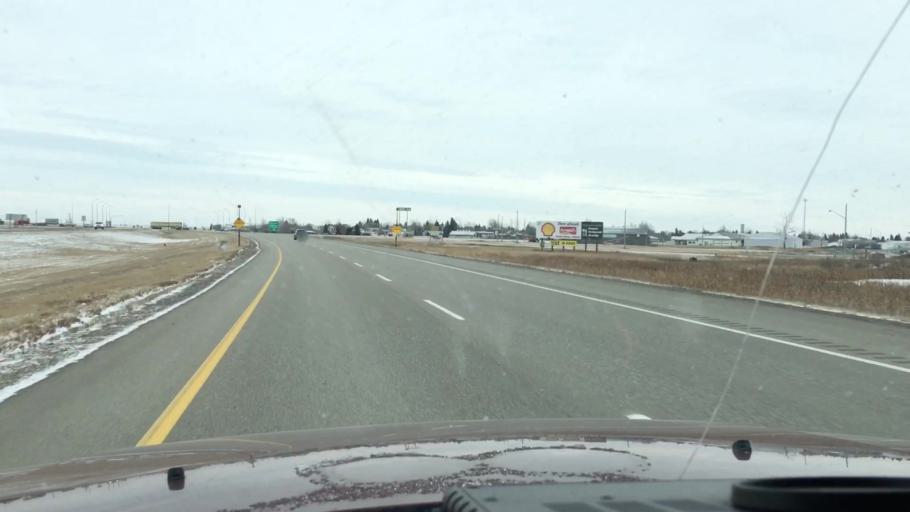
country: CA
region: Saskatchewan
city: Watrous
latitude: 51.2721
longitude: -106.0013
